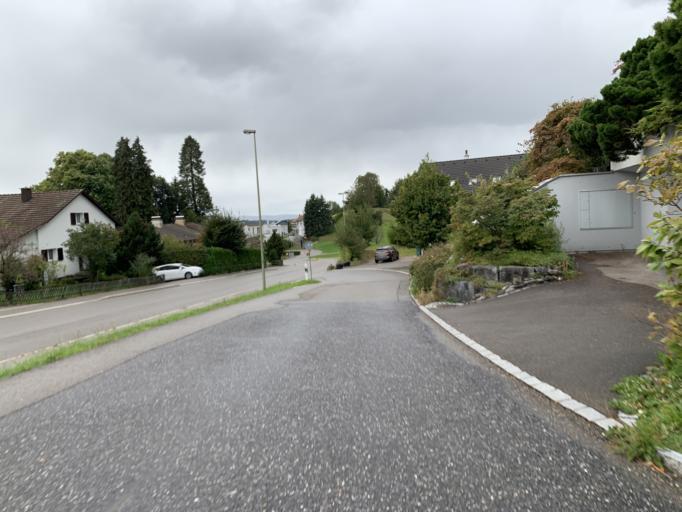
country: CH
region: Zurich
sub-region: Bezirk Hinwil
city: Hinwil
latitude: 47.3006
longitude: 8.8520
